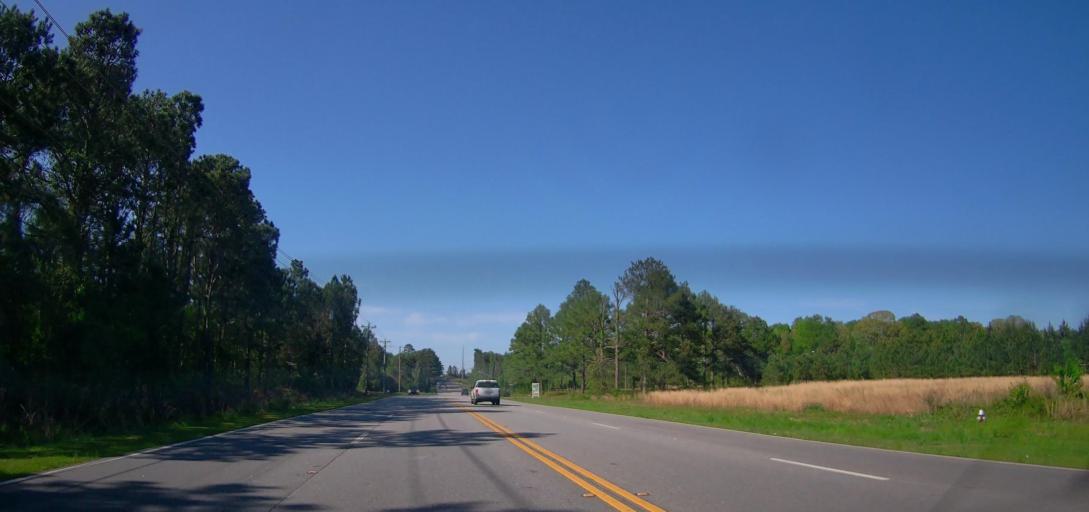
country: US
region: Georgia
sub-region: Houston County
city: Warner Robins
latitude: 32.6464
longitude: -83.6414
